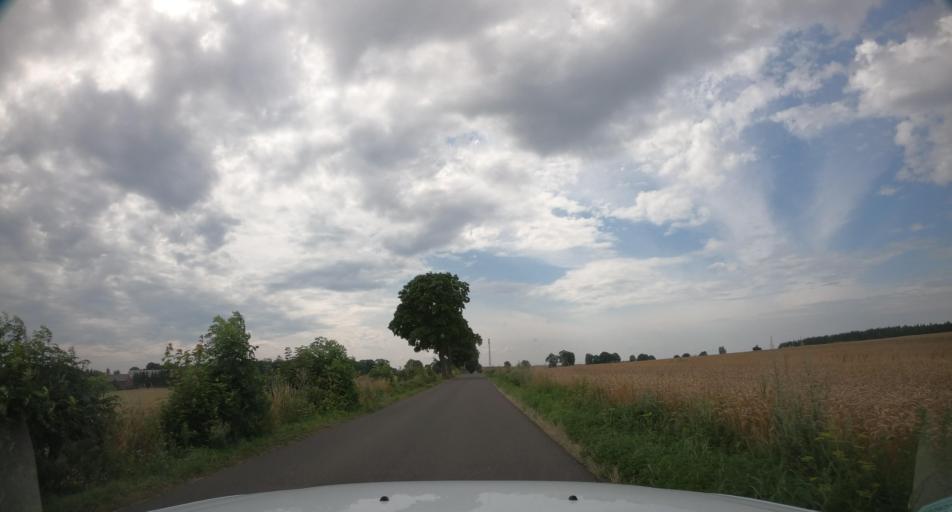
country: PL
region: West Pomeranian Voivodeship
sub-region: Powiat walecki
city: Walcz
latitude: 53.2342
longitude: 16.3215
